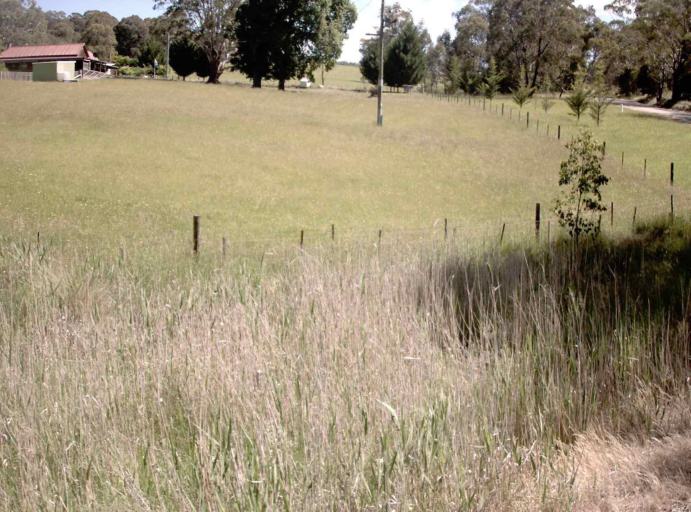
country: AU
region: New South Wales
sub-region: Bombala
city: Bombala
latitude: -37.0602
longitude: 148.8018
